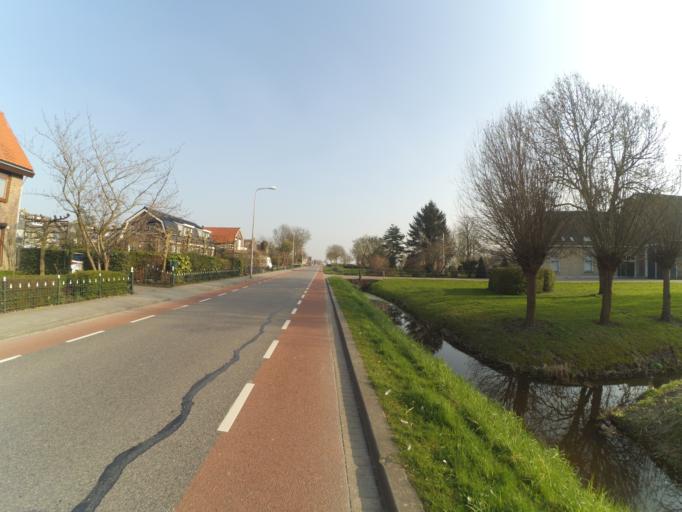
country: NL
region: South Holland
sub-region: Gemeente Spijkenisse
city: Spijkenisse
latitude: 51.8196
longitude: 4.2553
